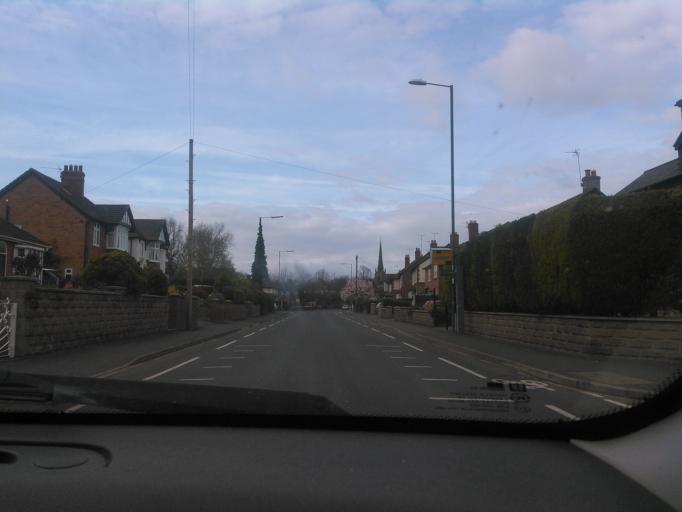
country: GB
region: England
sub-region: Shropshire
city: Shrewsbury
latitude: 52.7002
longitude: -2.7558
